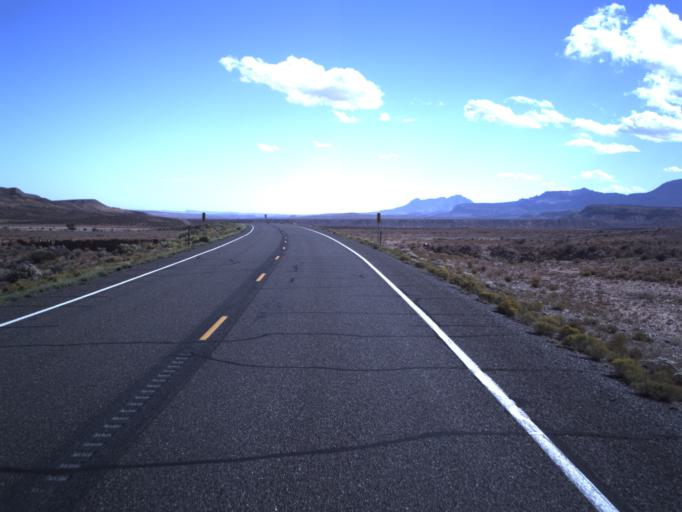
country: US
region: Utah
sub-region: Wayne County
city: Loa
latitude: 38.1008
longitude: -110.6233
